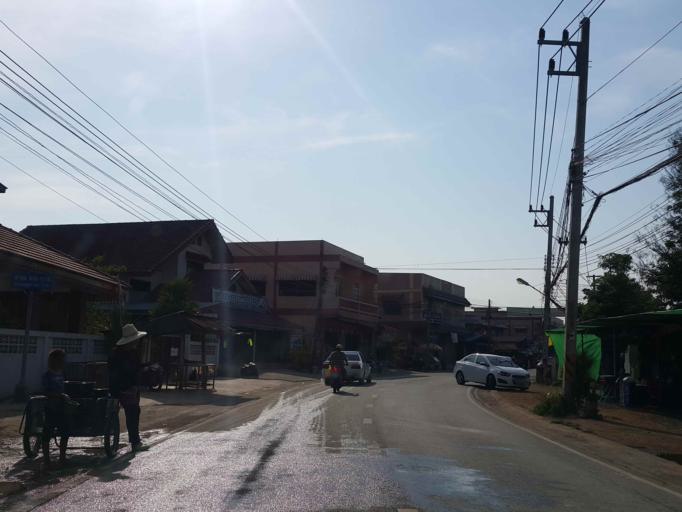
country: TH
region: Sukhothai
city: Thung Saliam
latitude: 17.3172
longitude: 99.5505
